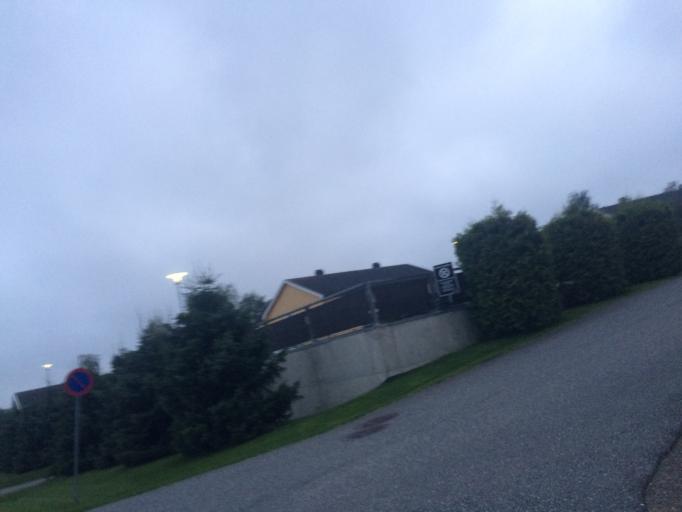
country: NO
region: Akershus
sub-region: Ski
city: Ski
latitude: 59.7187
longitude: 10.8291
